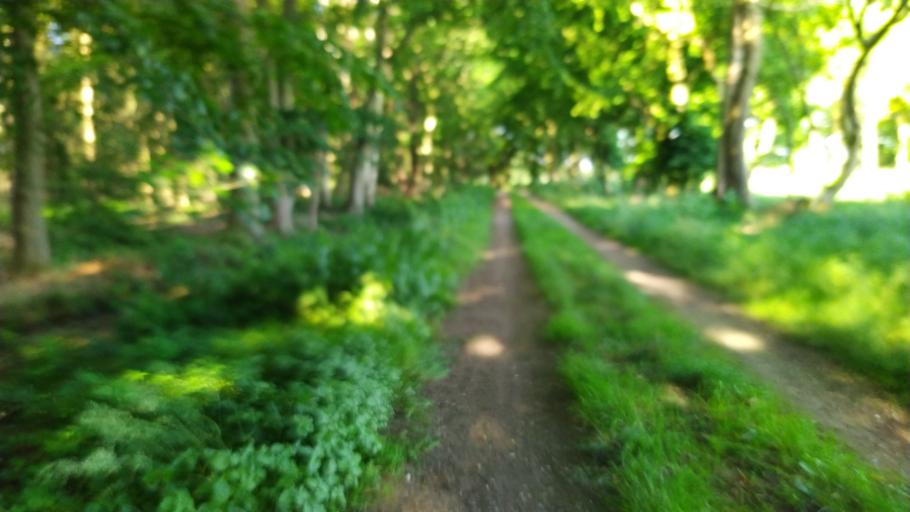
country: DE
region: Lower Saxony
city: Lintig
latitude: 53.5950
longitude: 8.9080
